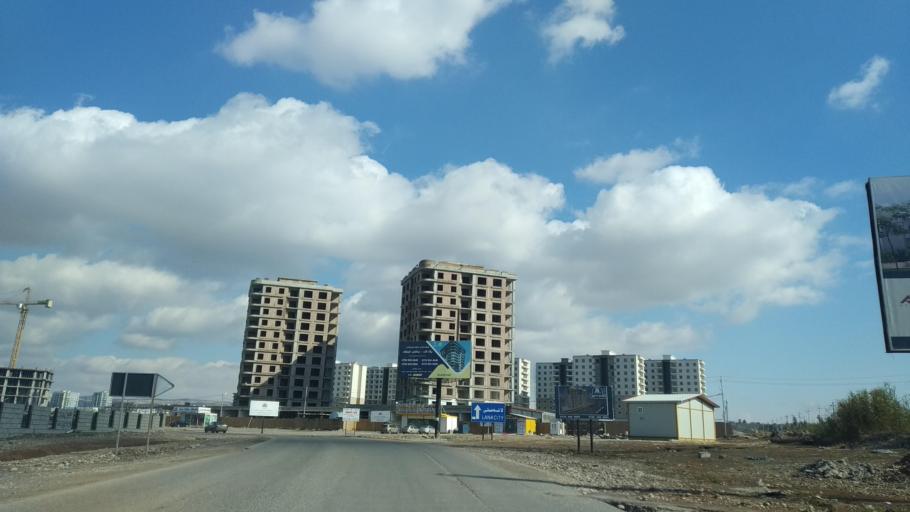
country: IQ
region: Arbil
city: Erbil
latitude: 36.2129
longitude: 44.1365
